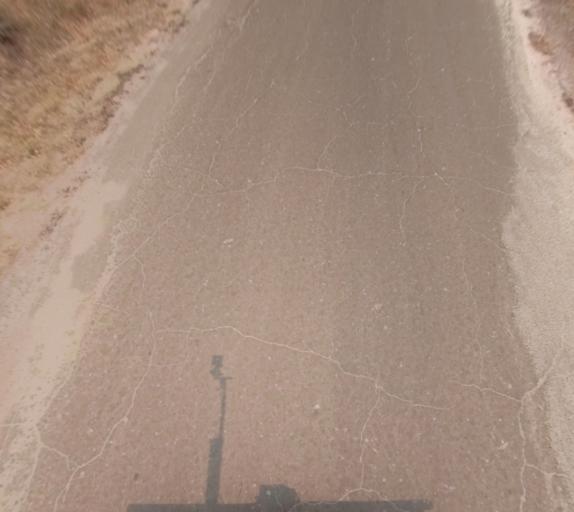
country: US
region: California
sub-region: Madera County
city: Oakhurst
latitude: 37.3382
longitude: -119.6517
